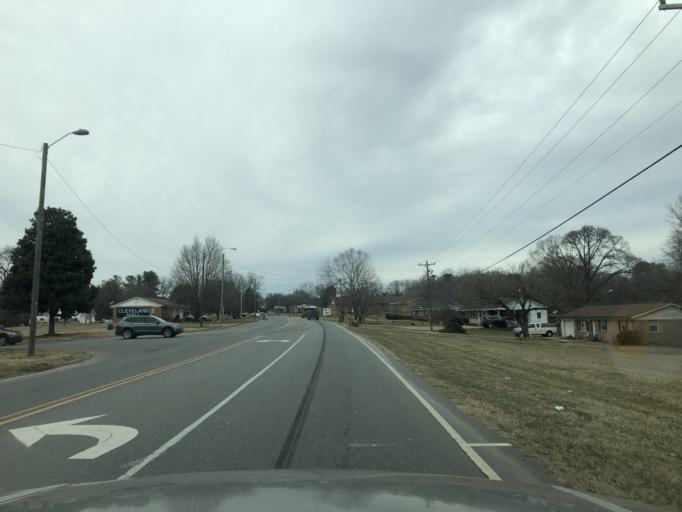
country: US
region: North Carolina
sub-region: Cleveland County
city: Shelby
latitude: 35.2706
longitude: -81.4806
